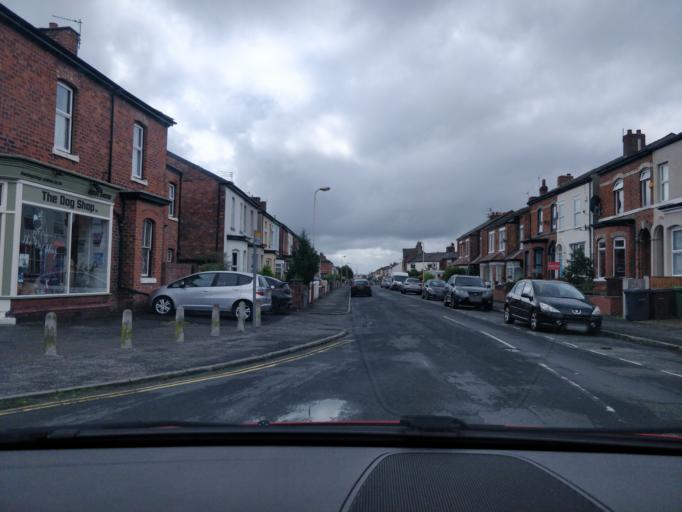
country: GB
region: England
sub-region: Sefton
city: Southport
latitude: 53.6491
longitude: -2.9905
